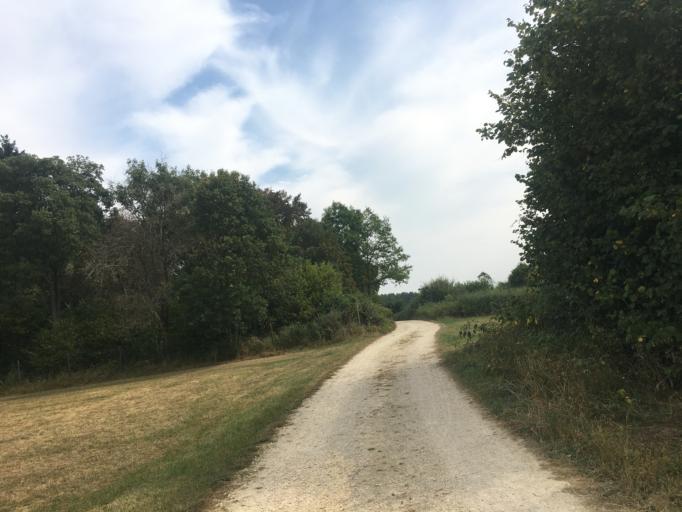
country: DE
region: Baden-Wuerttemberg
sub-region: Tuebingen Region
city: Hayingen
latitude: 48.2791
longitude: 9.4935
